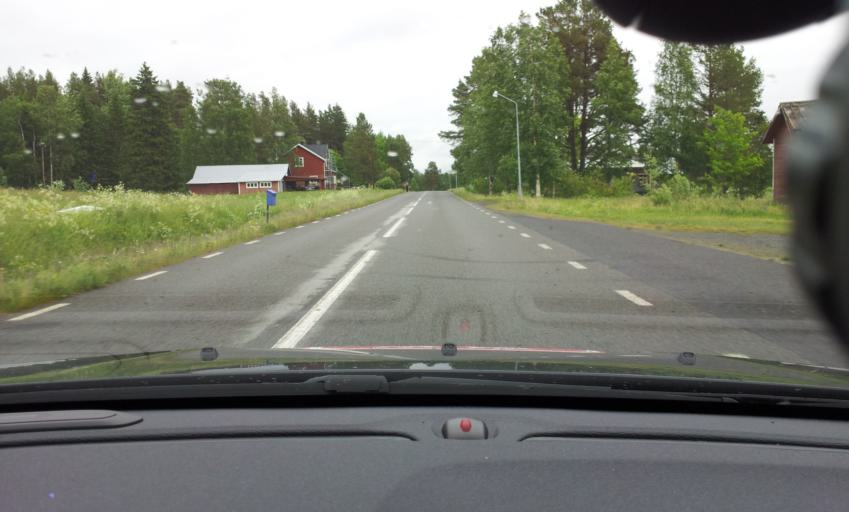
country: SE
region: Jaemtland
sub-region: OEstersunds Kommun
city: Lit
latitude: 63.7205
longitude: 14.9589
